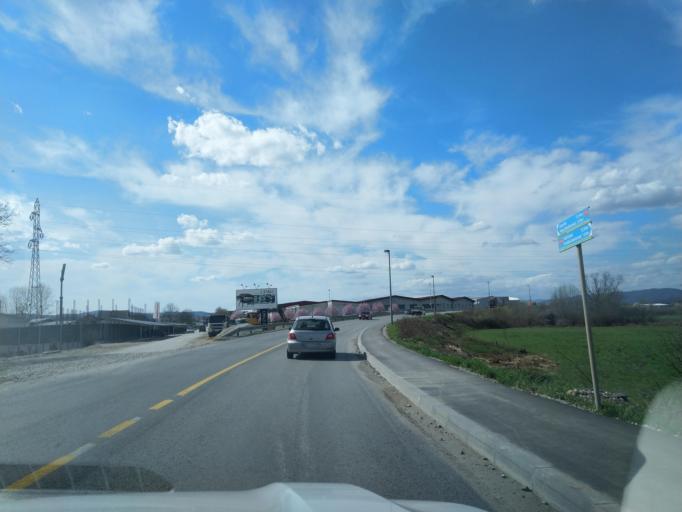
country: RS
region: Central Serbia
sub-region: Zlatiborski Okrug
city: Pozega
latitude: 43.8319
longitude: 20.0475
